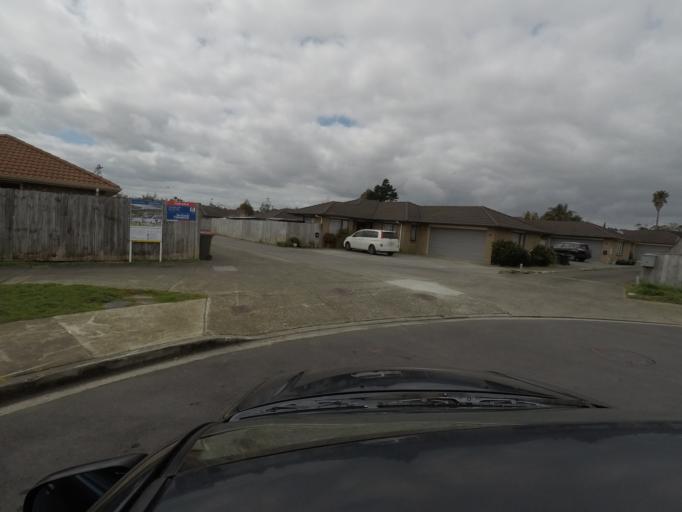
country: NZ
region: Auckland
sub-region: Auckland
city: Tamaki
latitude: -36.9327
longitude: 174.8563
